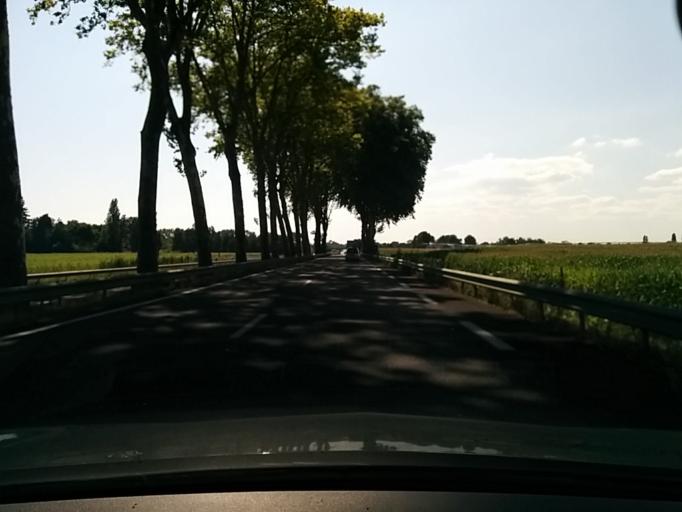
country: FR
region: Aquitaine
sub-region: Departement des Landes
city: Meilhan
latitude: 43.8649
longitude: -0.6604
